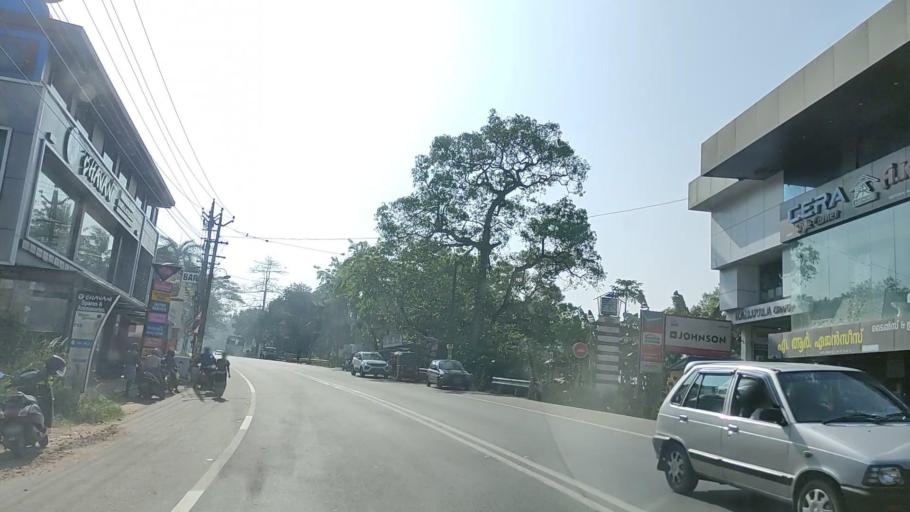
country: IN
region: Kerala
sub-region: Kollam
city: Punalur
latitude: 8.8928
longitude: 76.8643
